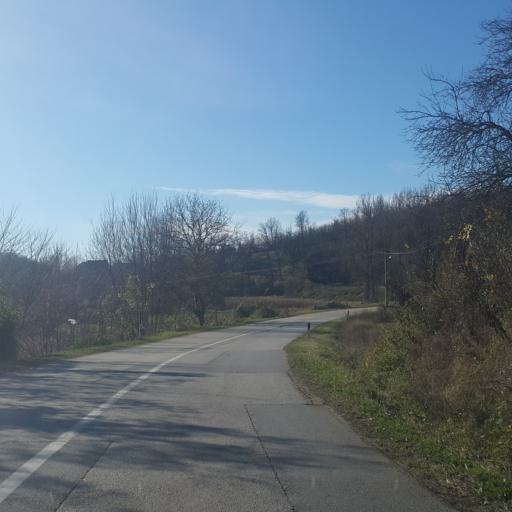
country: RS
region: Central Serbia
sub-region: Sumadijski Okrug
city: Raca
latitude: 44.2461
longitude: 20.8924
